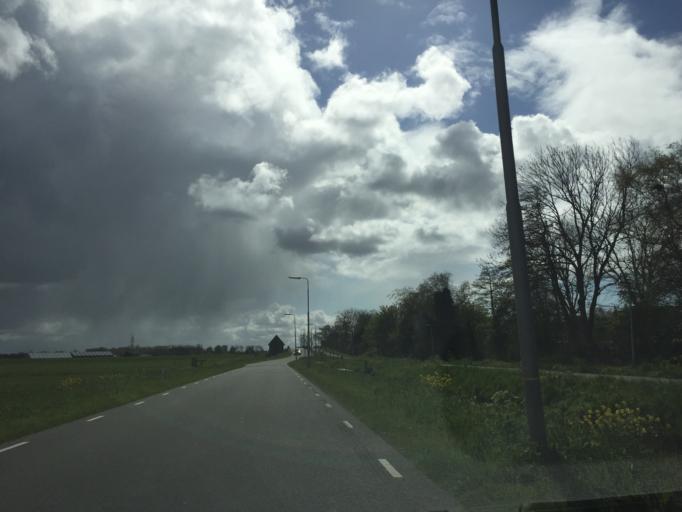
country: NL
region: South Holland
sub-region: Gemeente Leiderdorp
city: Leiderdorp
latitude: 52.1858
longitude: 4.5428
